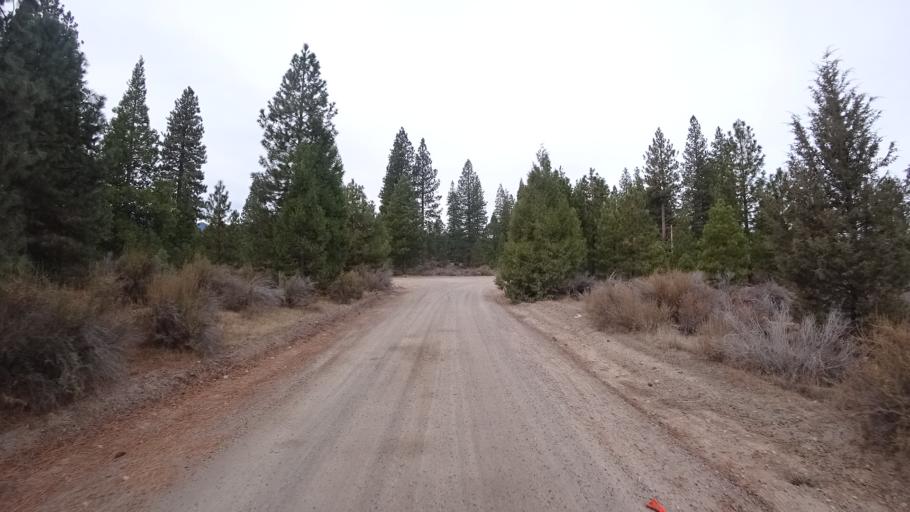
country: US
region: California
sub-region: Siskiyou County
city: Weed
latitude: 41.3938
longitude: -122.3725
